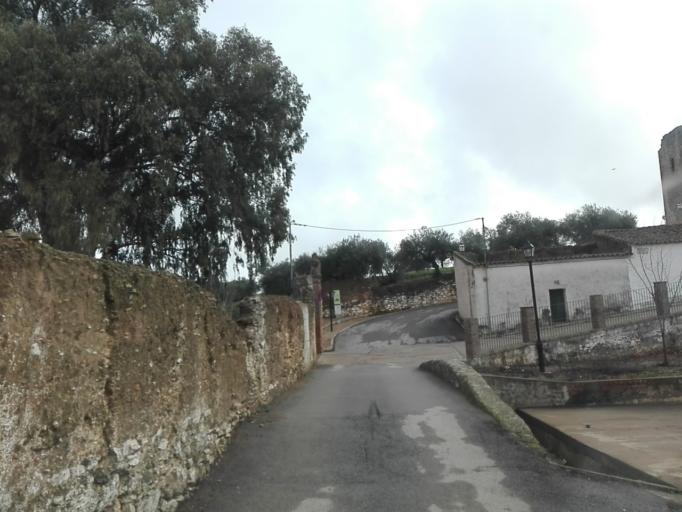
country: ES
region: Extremadura
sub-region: Provincia de Badajoz
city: Villagarcia de la Torre
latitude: 38.2959
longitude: -6.0792
